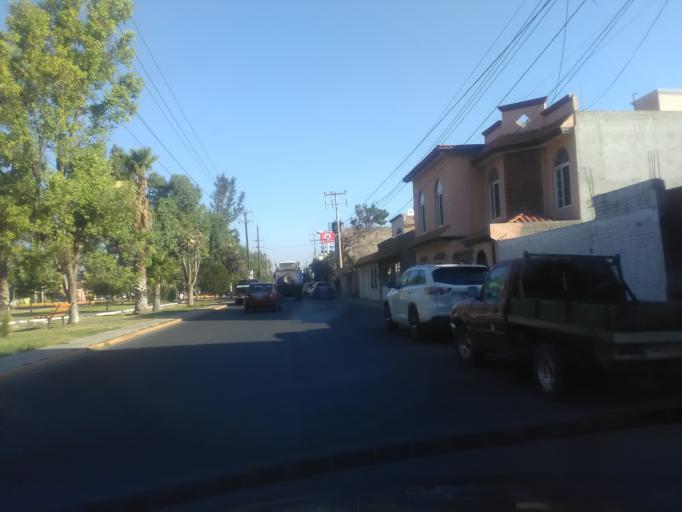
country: MX
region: Durango
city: Victoria de Durango
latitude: 24.0427
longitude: -104.6335
